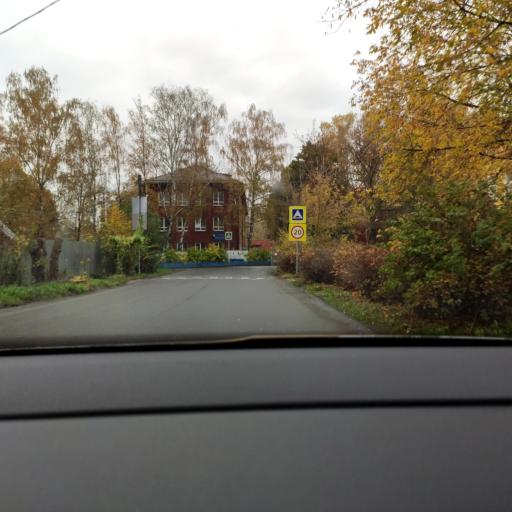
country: RU
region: Moskovskaya
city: Druzhba
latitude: 55.8877
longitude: 37.7542
